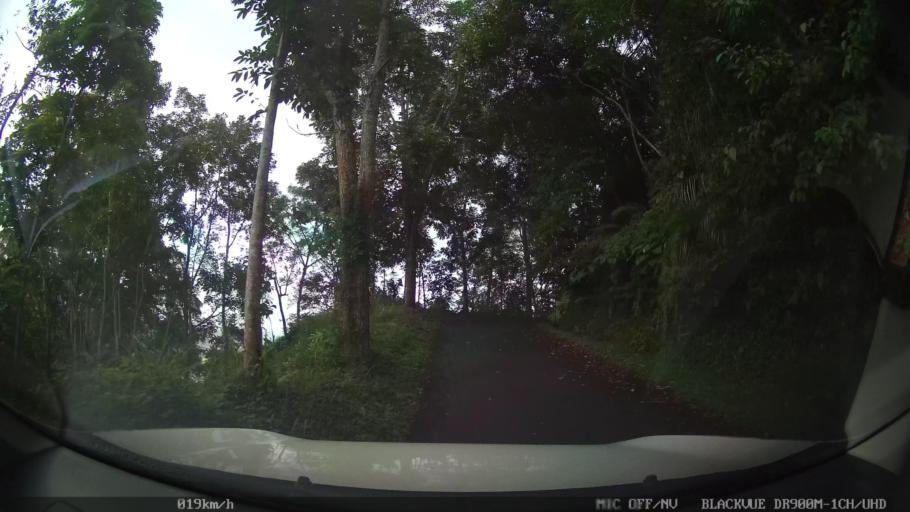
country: ID
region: Bali
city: Peneng
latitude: -8.3642
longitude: 115.2098
